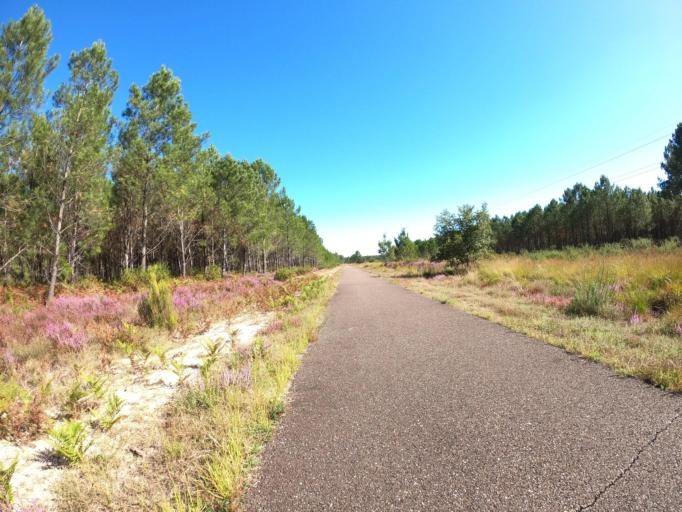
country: FR
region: Aquitaine
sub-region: Departement des Landes
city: Ychoux
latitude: 44.3389
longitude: -0.9605
